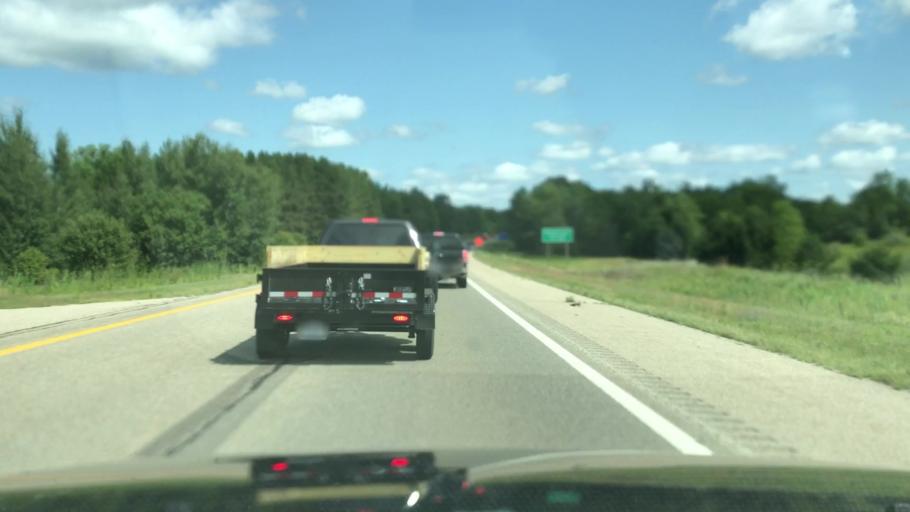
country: US
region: Michigan
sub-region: Mecosta County
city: Big Rapids
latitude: 43.7289
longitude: -85.5326
